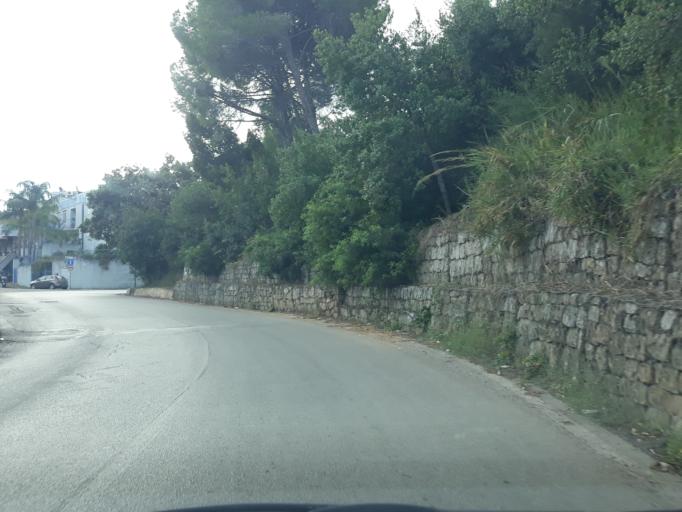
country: IT
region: Sicily
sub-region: Palermo
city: Cefalu
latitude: 38.0300
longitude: 14.0018
